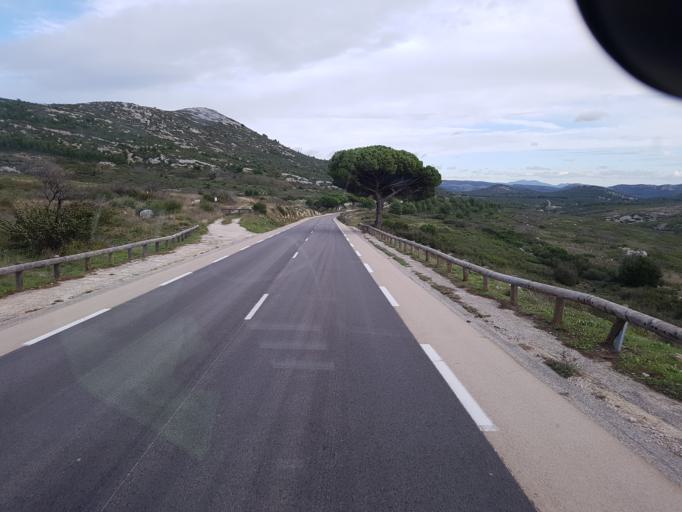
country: FR
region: Provence-Alpes-Cote d'Azur
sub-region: Departement des Bouches-du-Rhone
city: Marseille 11
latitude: 43.2387
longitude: 5.4716
